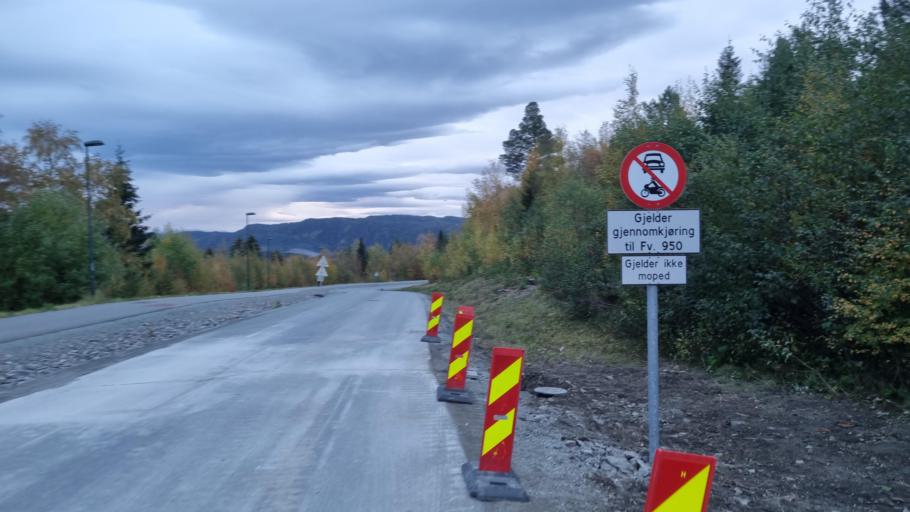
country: NO
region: Sor-Trondelag
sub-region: Malvik
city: Hommelvik
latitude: 63.4228
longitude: 10.7630
